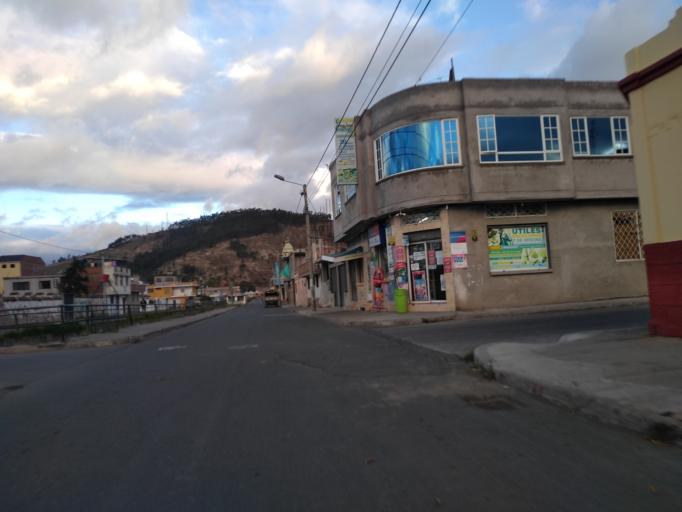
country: EC
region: Chimborazo
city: Riobamba
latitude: -1.6880
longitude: -78.6774
